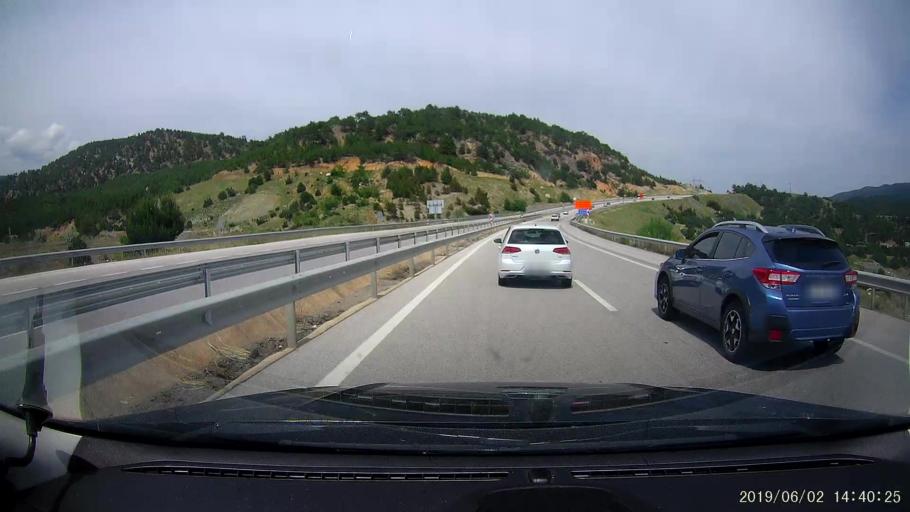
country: TR
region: Corum
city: Hacihamza
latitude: 41.0824
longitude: 34.3182
